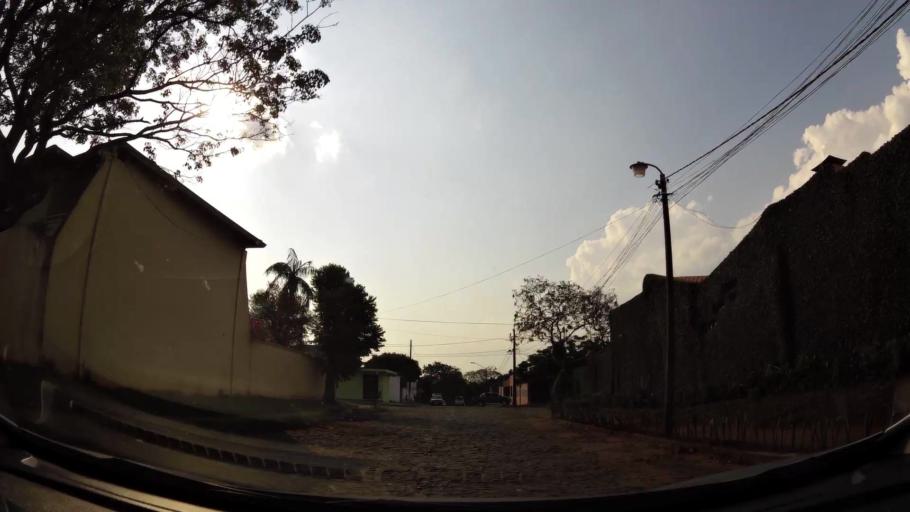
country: PY
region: Alto Parana
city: Presidente Franco
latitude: -25.5341
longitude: -54.6318
